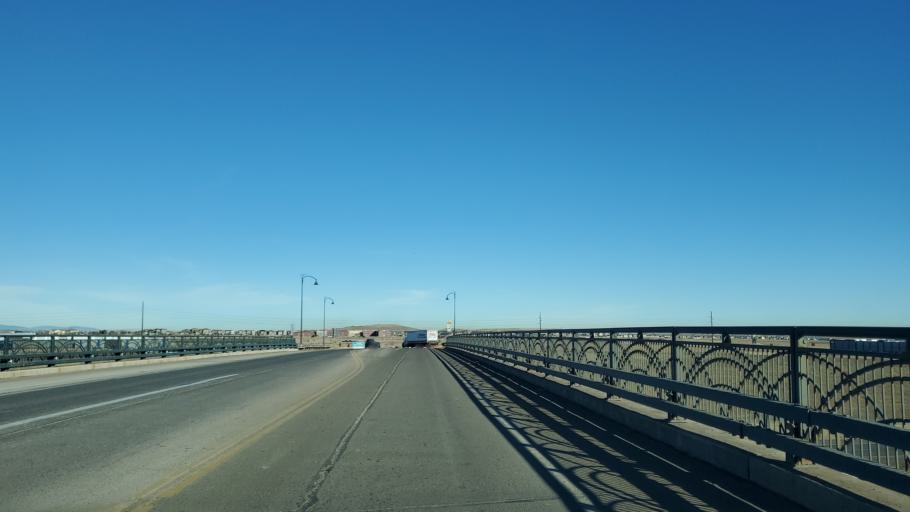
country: US
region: Colorado
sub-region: Boulder County
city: Erie
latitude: 39.9851
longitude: -105.0170
